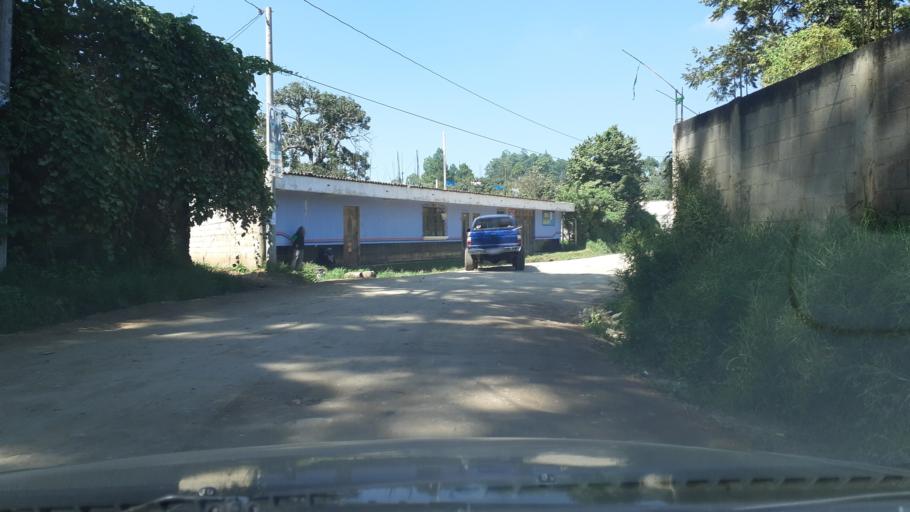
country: GT
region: Chimaltenango
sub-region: Municipio de Chimaltenango
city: Chimaltenango
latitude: 14.6688
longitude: -90.8367
